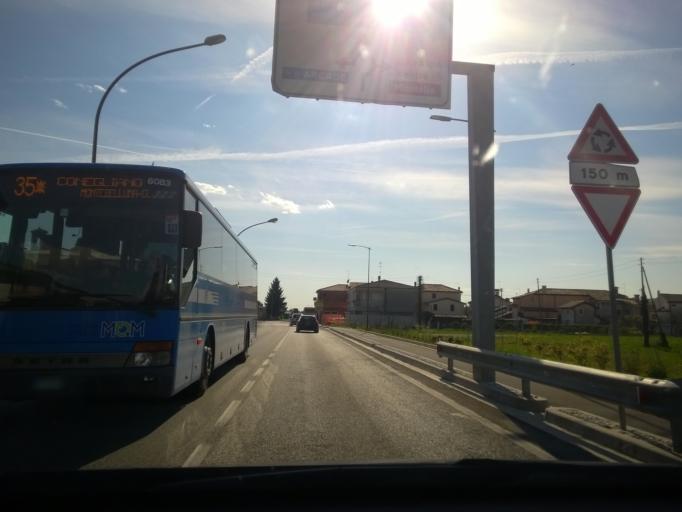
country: IT
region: Veneto
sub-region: Provincia di Treviso
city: Nervesa della Battaglia
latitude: 45.8049
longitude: 12.1887
